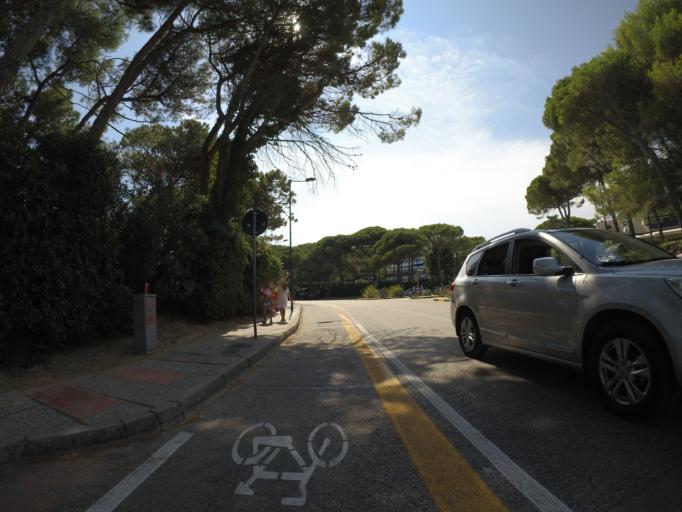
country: IT
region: Friuli Venezia Giulia
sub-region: Provincia di Udine
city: Lignano Sabbiadoro
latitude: 45.6534
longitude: 13.1022
